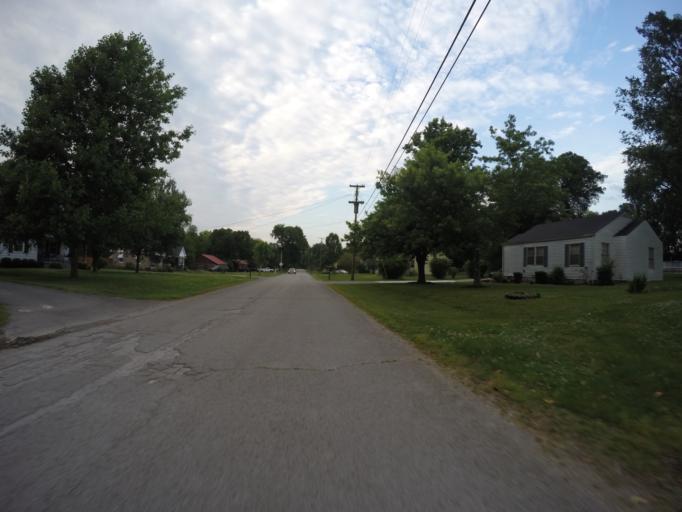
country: US
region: Tennessee
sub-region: Davidson County
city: Lakewood
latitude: 36.2415
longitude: -86.6291
